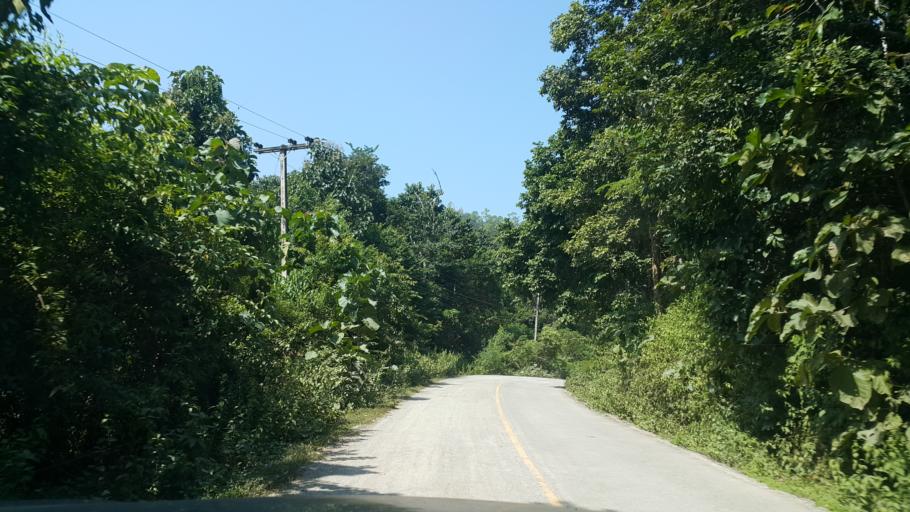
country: TH
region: Chiang Mai
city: Samoeng
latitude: 18.8916
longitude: 98.5996
